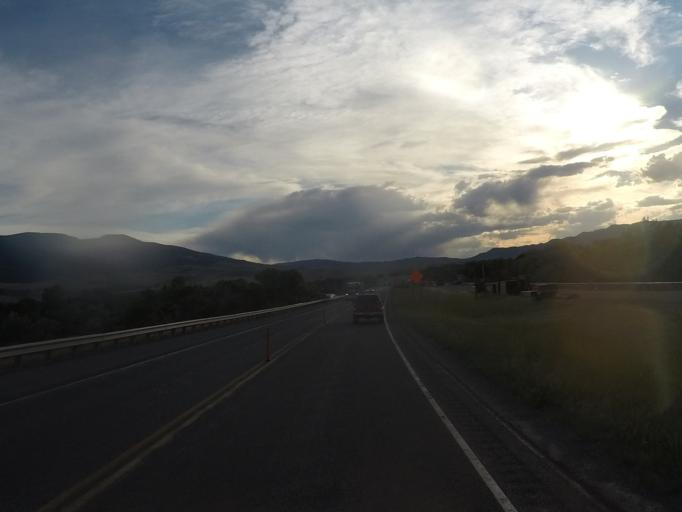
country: US
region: Montana
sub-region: Park County
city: Livingston
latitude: 45.6444
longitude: -110.5568
